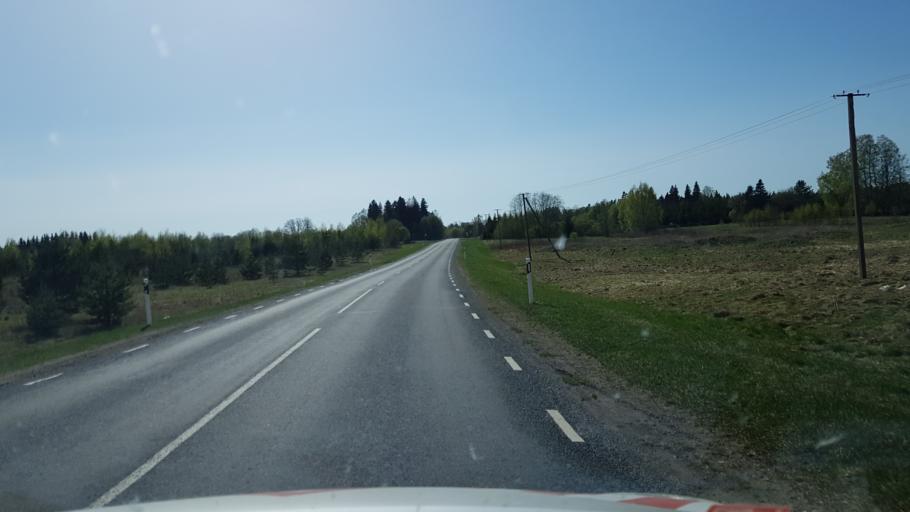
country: EE
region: Viljandimaa
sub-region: Viljandi linn
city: Viljandi
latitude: 58.3129
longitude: 25.5606
